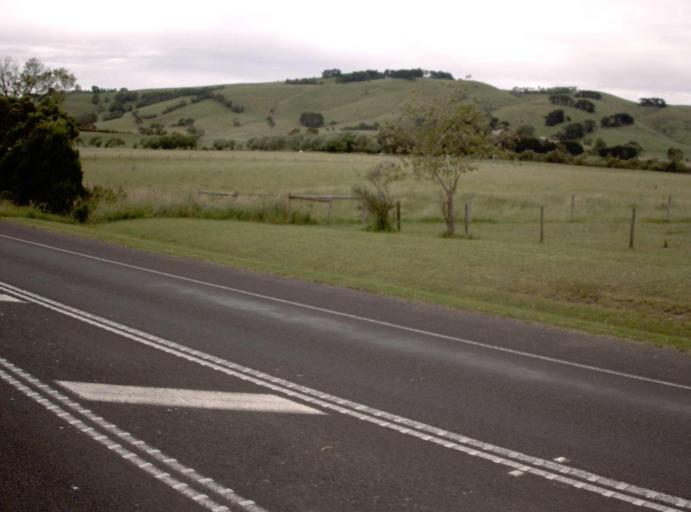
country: AU
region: Victoria
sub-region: Bass Coast
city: North Wonthaggi
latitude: -38.3713
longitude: 145.6756
